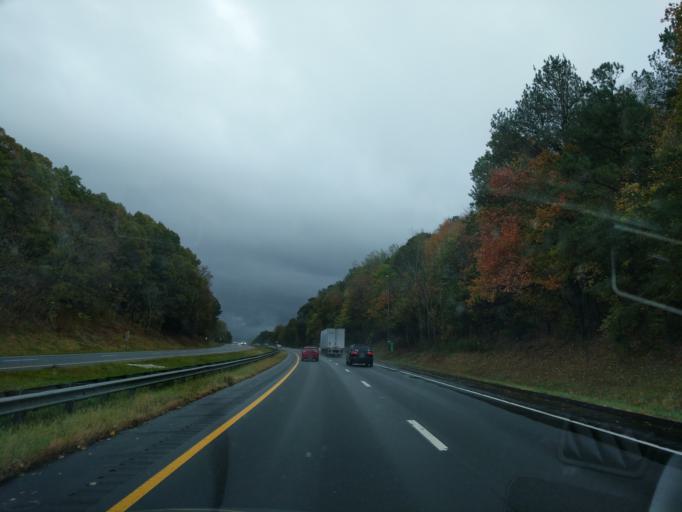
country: US
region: North Carolina
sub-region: Orange County
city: Hillsborough
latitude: 36.0392
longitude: -79.0246
